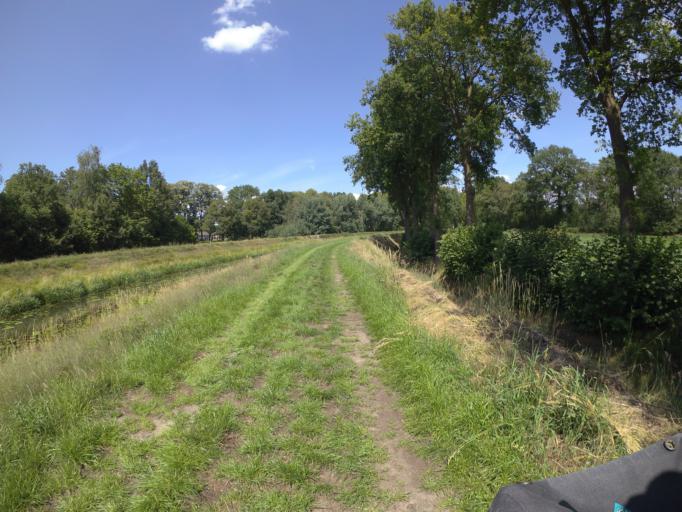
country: NL
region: North Brabant
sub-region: Gemeente Sint-Michielsgestel
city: Sint-Michielsgestel
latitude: 51.6988
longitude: 5.3728
